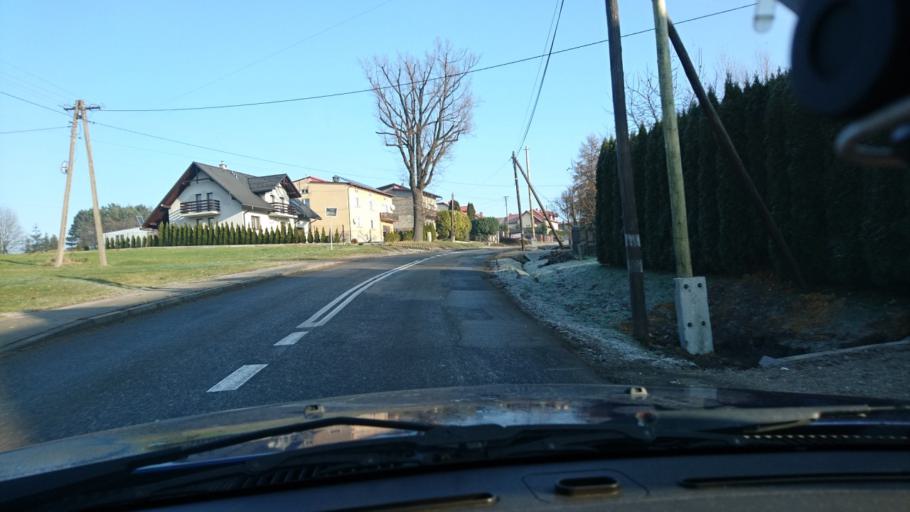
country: PL
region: Silesian Voivodeship
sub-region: Powiat bielski
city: Bestwina
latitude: 49.9005
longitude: 19.0747
